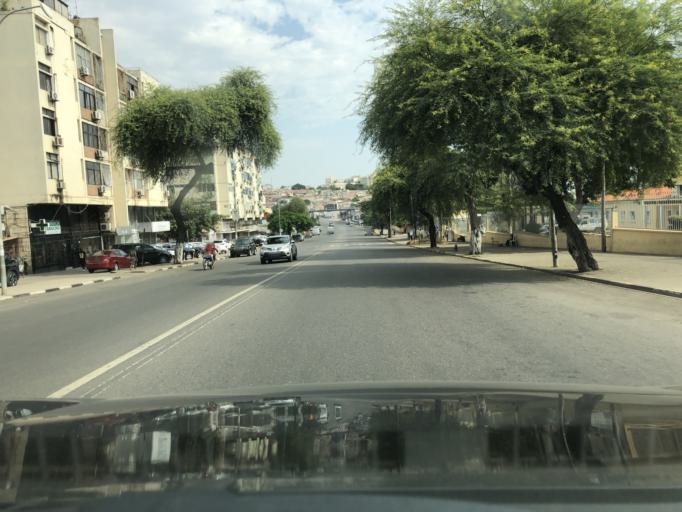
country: AO
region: Luanda
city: Luanda
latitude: -8.8271
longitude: 13.2270
